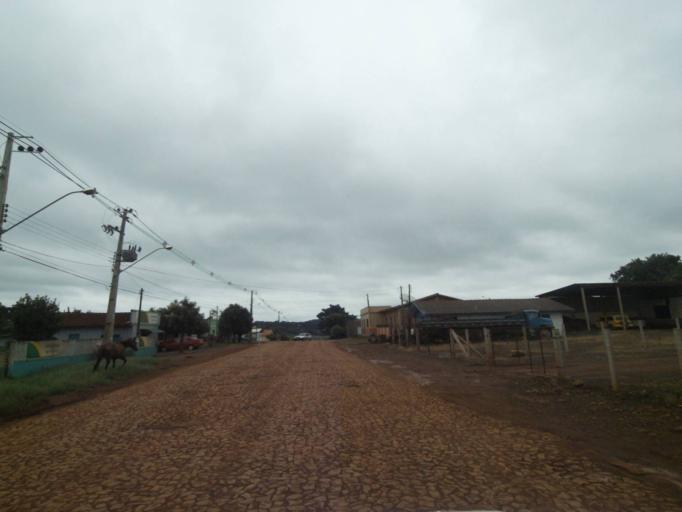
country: BR
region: Parana
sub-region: Pitanga
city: Pitanga
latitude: -24.9408
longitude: -51.8722
